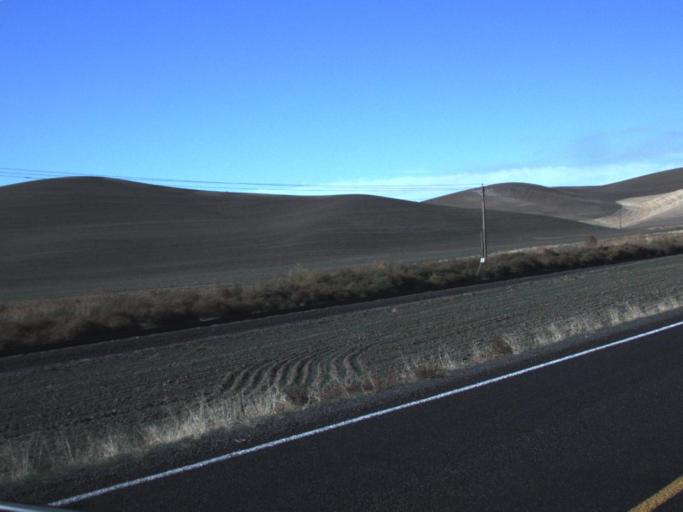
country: US
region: Washington
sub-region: Walla Walla County
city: Walla Walla
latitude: 46.2185
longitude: -118.3928
